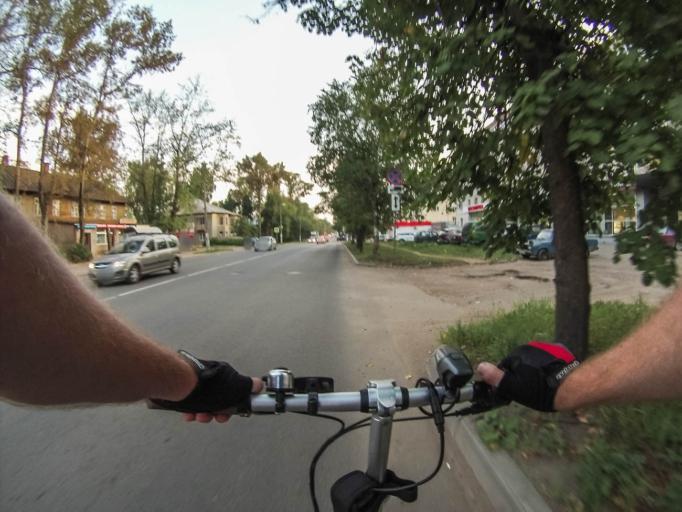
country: RU
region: Kostroma
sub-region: Kostromskoy Rayon
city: Kostroma
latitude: 57.7918
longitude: 40.9461
